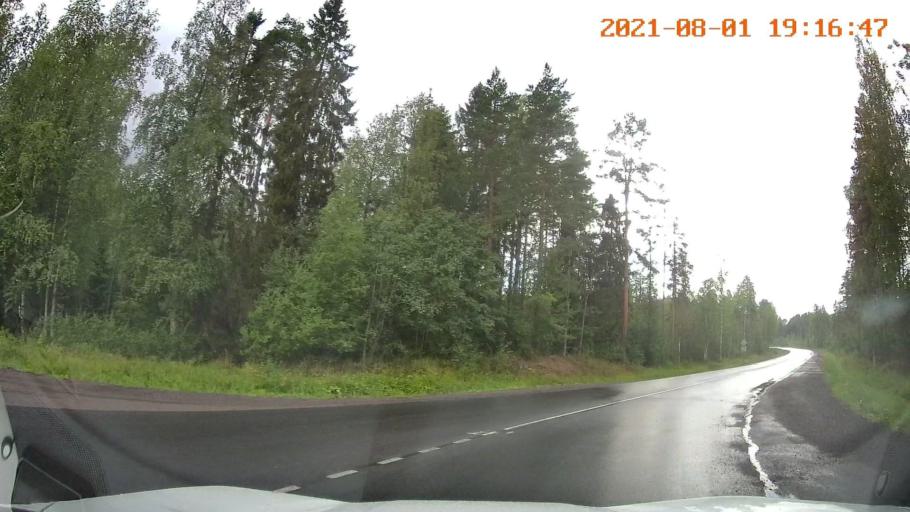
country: RU
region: Leningrad
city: Podporozh'ye
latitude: 60.8824
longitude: 34.1678
